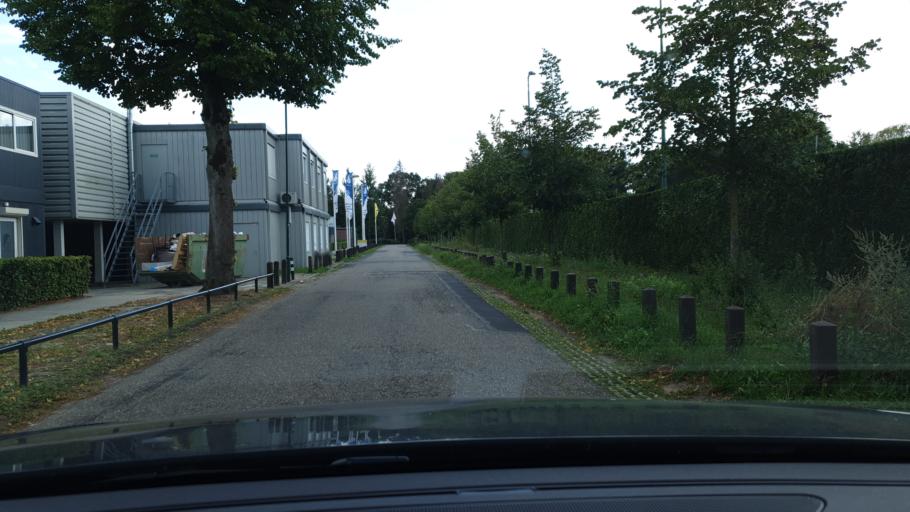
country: NL
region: North Brabant
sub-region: Gemeente Eindhoven
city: Eindhoven
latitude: 51.4122
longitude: 5.4784
